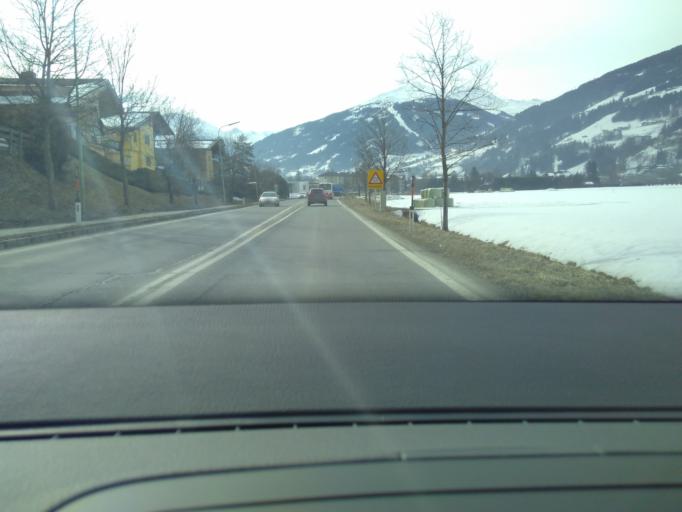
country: AT
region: Salzburg
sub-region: Politischer Bezirk Sankt Johann im Pongau
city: Bad Hofgastein
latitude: 47.1818
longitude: 13.1016
